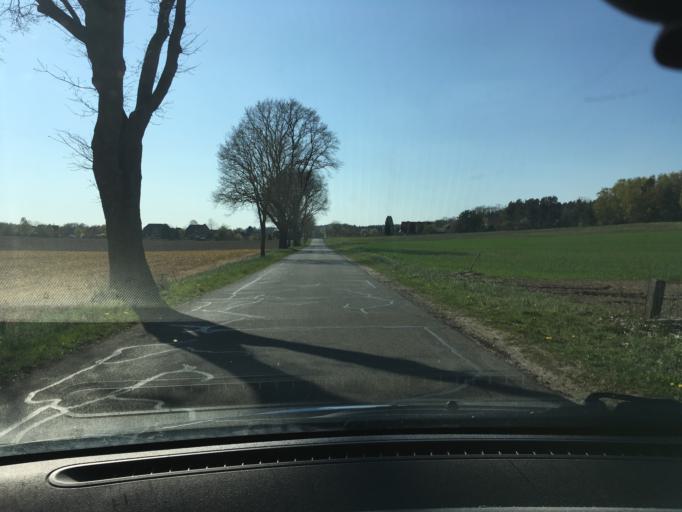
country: DE
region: Lower Saxony
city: Hitzacker
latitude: 53.1524
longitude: 11.0112
